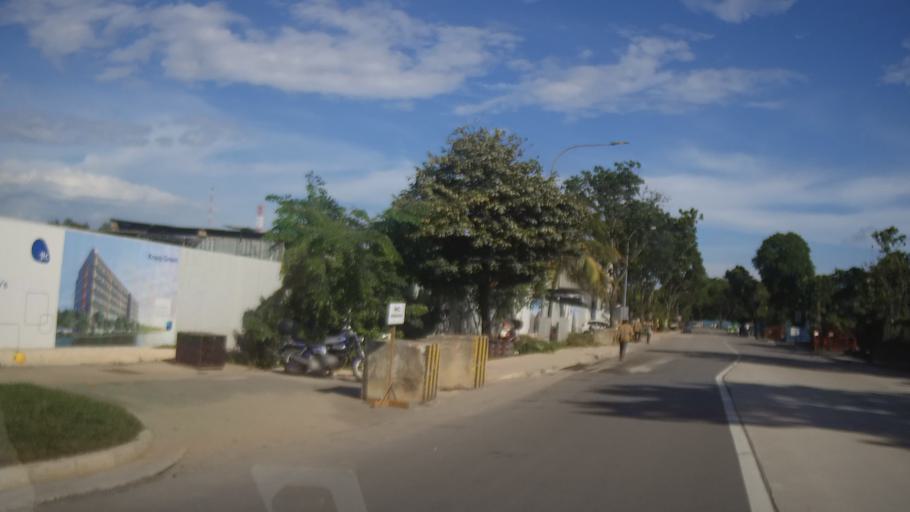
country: MY
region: Johor
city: Johor Bahru
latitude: 1.4365
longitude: 103.7581
